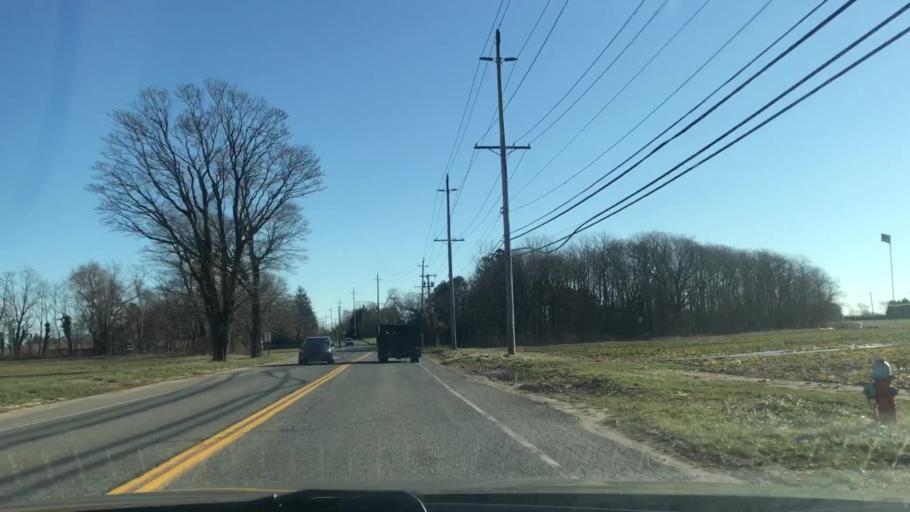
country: US
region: New York
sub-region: Suffolk County
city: Northville
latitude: 40.9680
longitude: -72.6433
